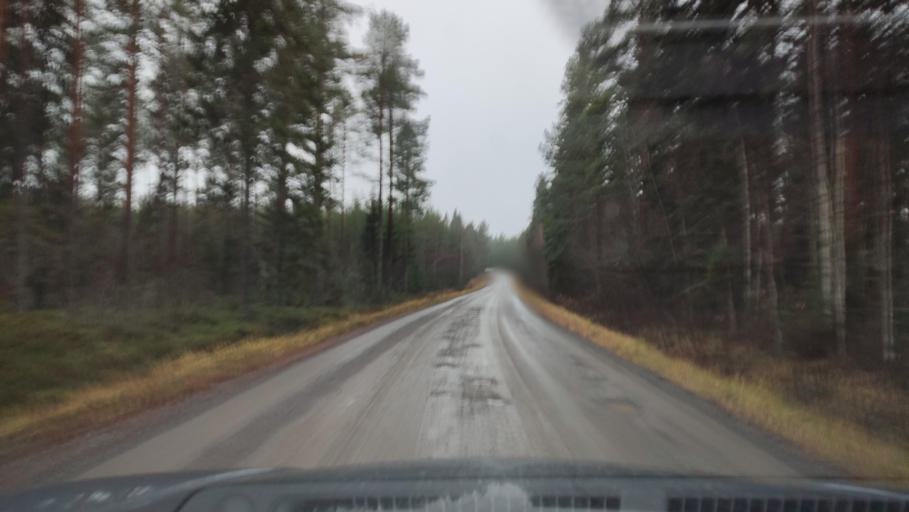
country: FI
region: Southern Ostrobothnia
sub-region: Suupohja
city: Karijoki
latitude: 62.1369
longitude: 21.6646
